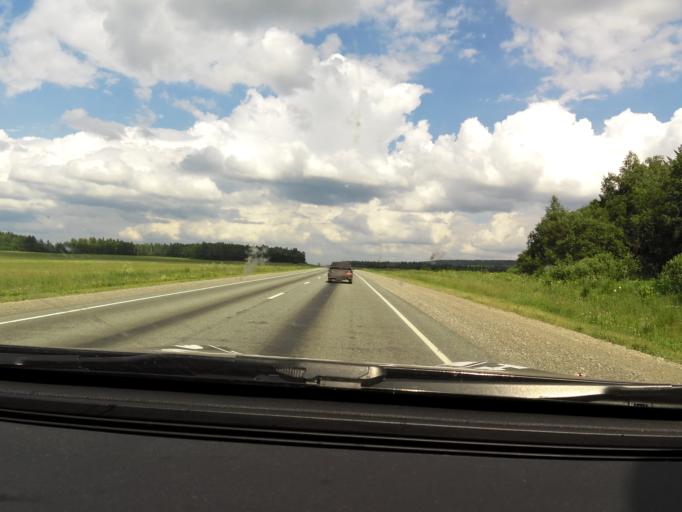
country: RU
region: Sverdlovsk
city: Bisert'
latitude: 56.8098
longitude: 58.7310
